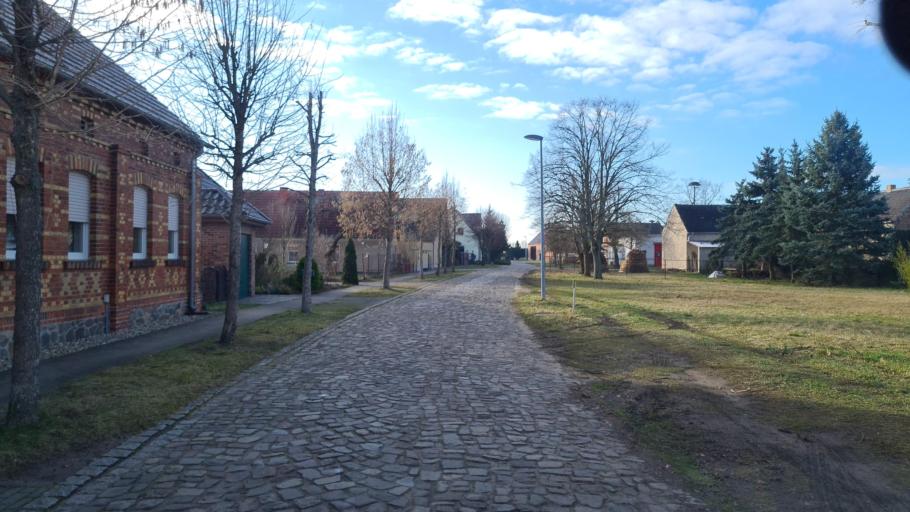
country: DE
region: Brandenburg
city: Herzberg
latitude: 51.7150
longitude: 13.2070
